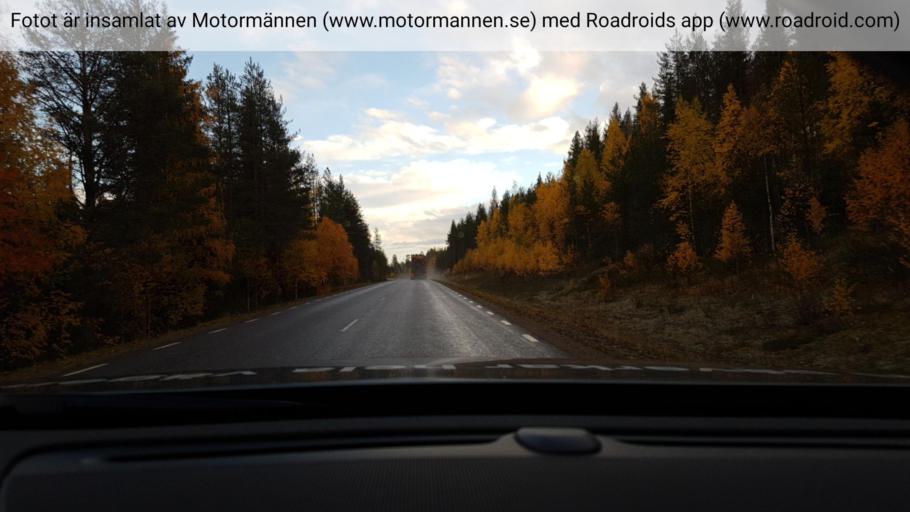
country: SE
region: Norrbotten
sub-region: Overkalix Kommun
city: OEverkalix
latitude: 66.6576
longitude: 22.6889
